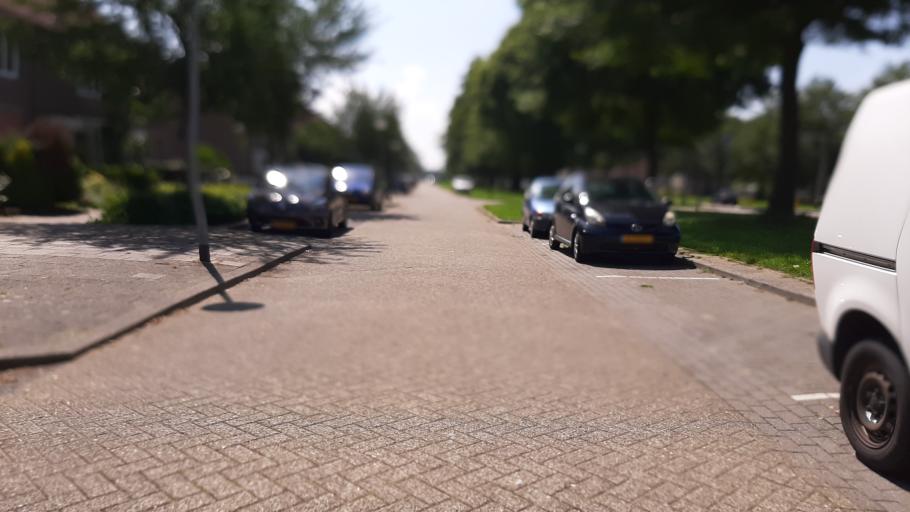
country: NL
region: Flevoland
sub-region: Gemeente Zeewolde
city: Zeewolde
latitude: 52.3285
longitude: 5.5394
